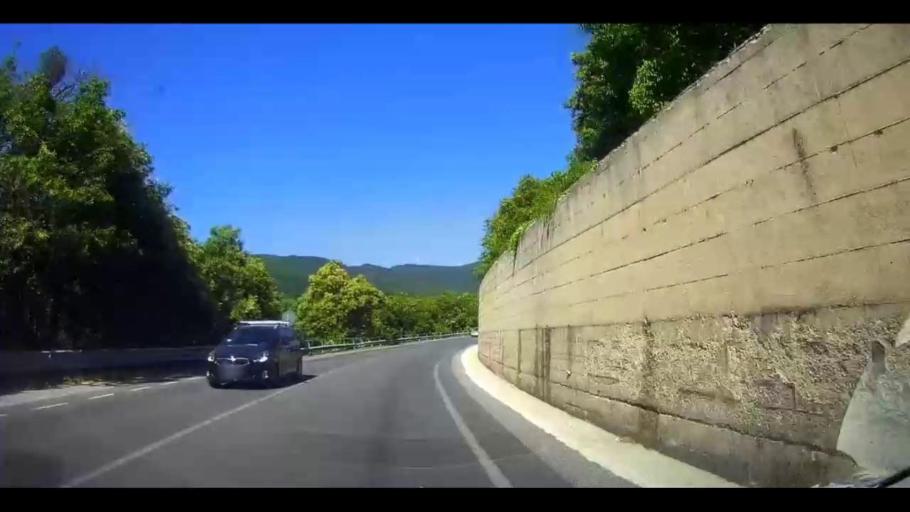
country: IT
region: Calabria
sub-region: Provincia di Cosenza
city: Celico
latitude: 39.3137
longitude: 16.3557
